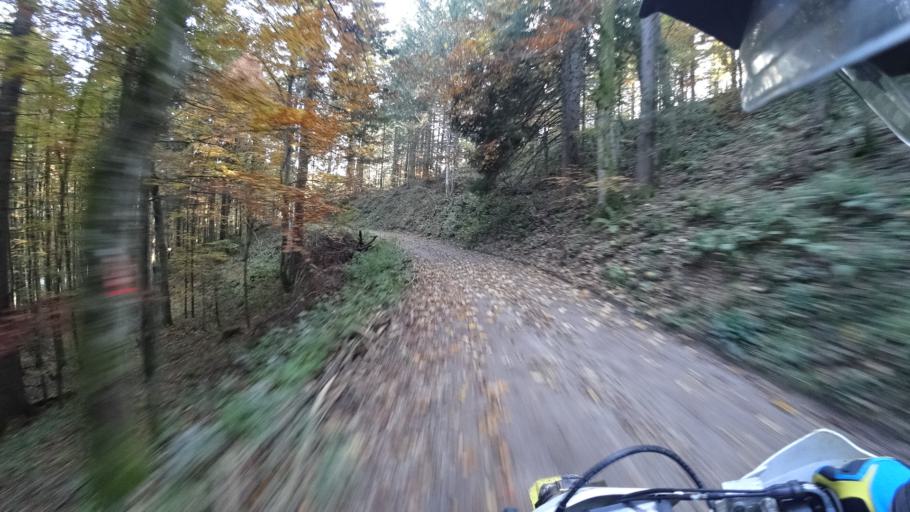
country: HR
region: Licko-Senjska
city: Jezerce
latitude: 44.9297
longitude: 15.4626
